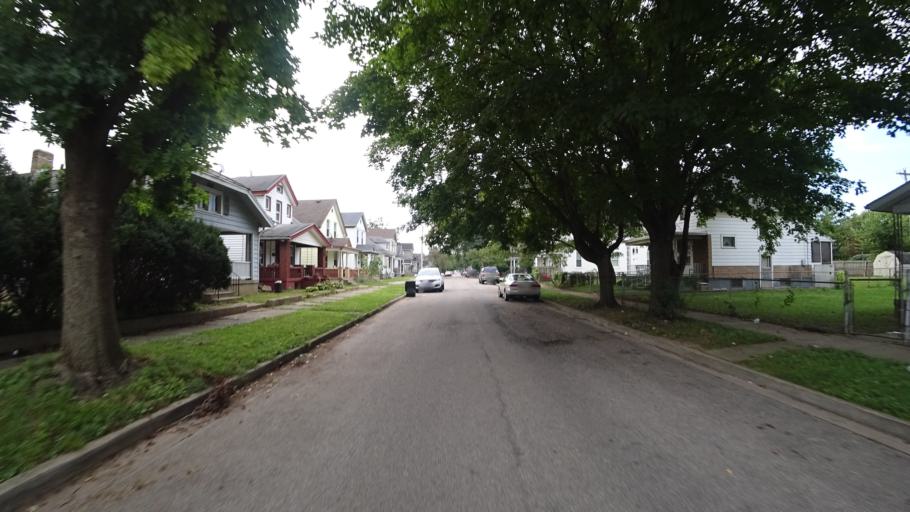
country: US
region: Ohio
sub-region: Butler County
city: Hamilton
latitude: 39.3961
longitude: -84.5470
